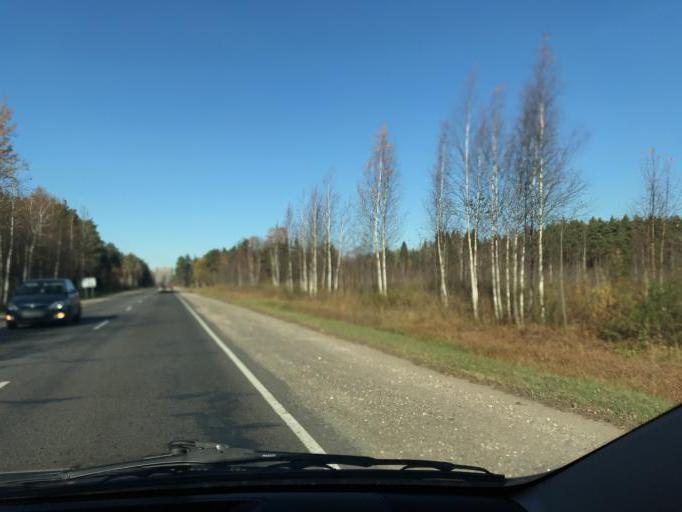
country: BY
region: Vitebsk
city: Polatsk
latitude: 55.5092
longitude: 28.7442
